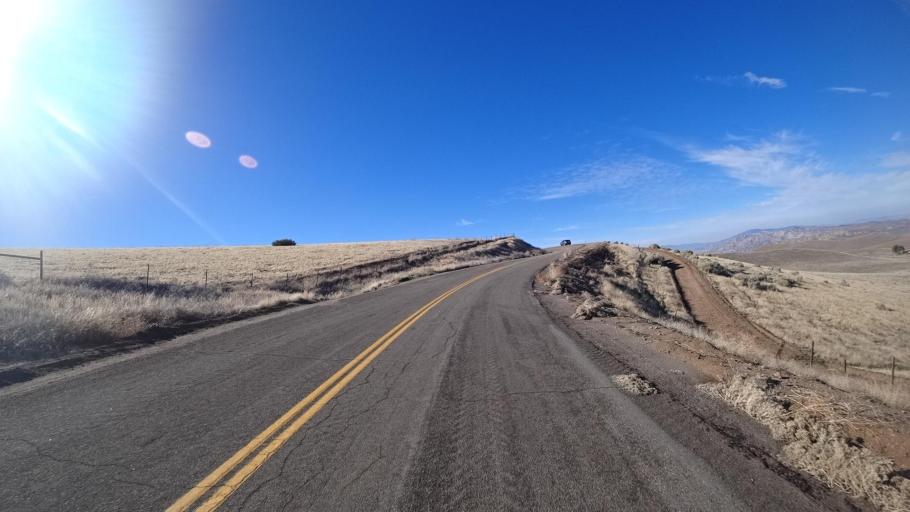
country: US
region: California
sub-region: Kern County
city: Maricopa
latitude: 34.9206
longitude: -119.4112
